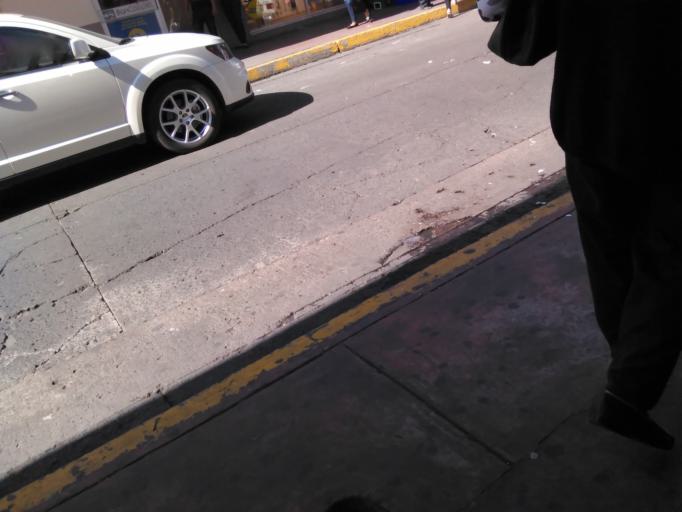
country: MX
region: Nayarit
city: Tepic
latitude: 21.5112
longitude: -104.8937
